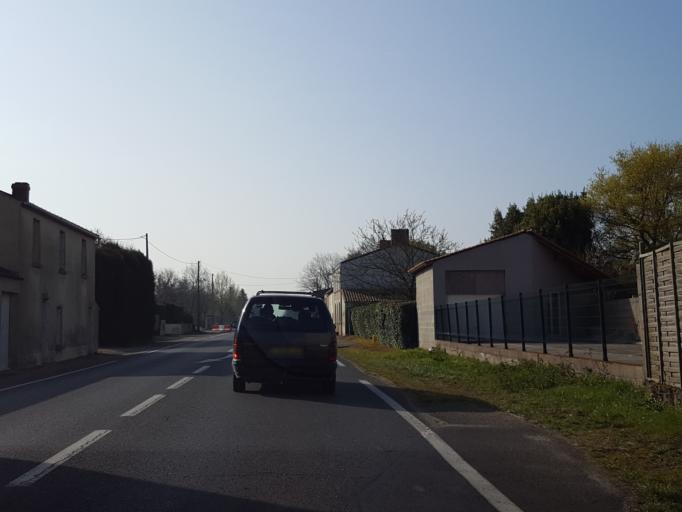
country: FR
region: Pays de la Loire
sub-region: Departement de la Loire-Atlantique
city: Geneston
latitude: 47.0897
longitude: -1.5291
